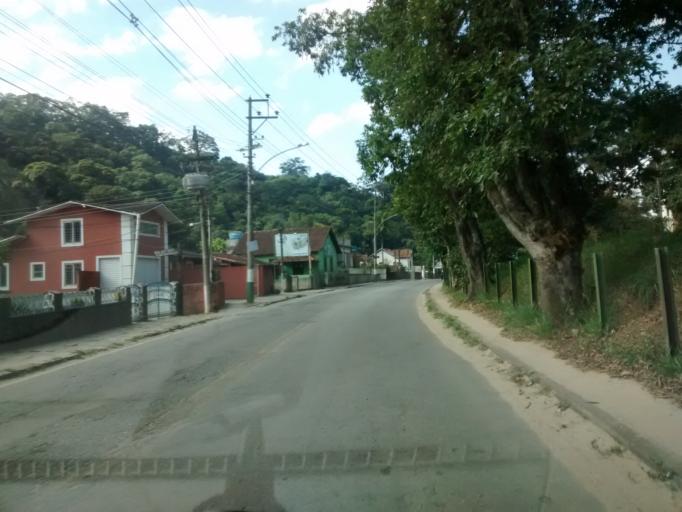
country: BR
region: Rio de Janeiro
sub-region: Miguel Pereira
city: Miguel Pereira
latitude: -22.4583
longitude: -43.4783
